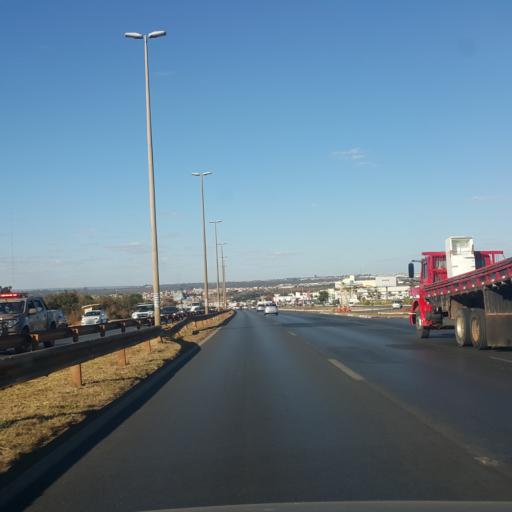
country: BR
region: Federal District
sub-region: Brasilia
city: Brasilia
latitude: -15.7903
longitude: -48.0240
